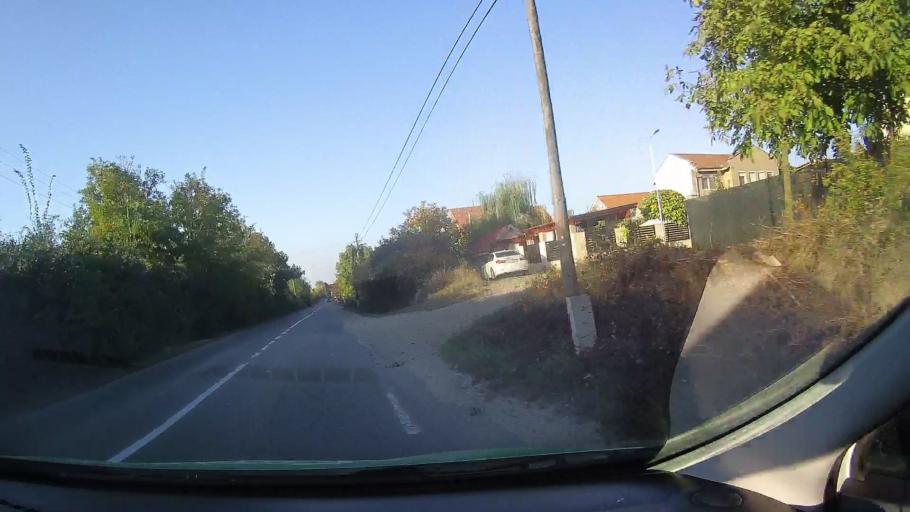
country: RO
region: Bihor
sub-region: Comuna Paleu
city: Paleu
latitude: 47.1054
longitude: 21.9286
